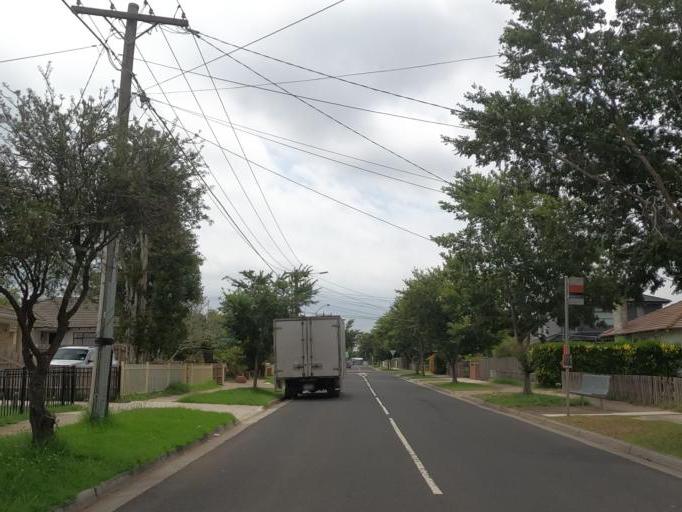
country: AU
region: Victoria
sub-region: Hume
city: Broadmeadows
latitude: -37.6891
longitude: 144.9226
